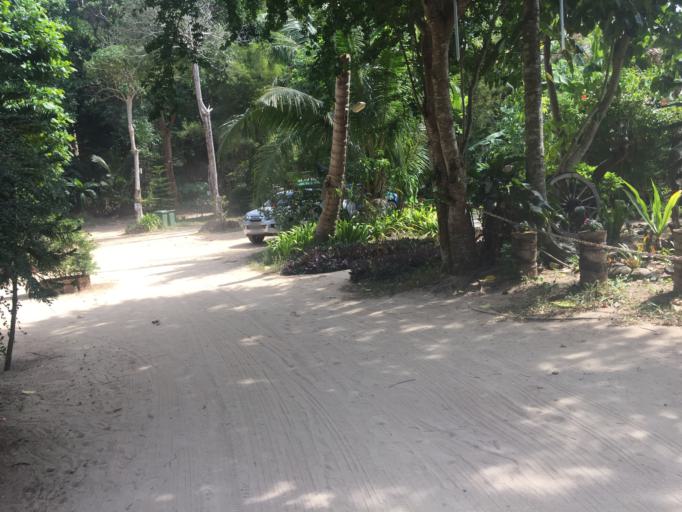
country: TH
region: Trat
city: Laem Ngop
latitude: 12.1167
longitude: 102.2657
